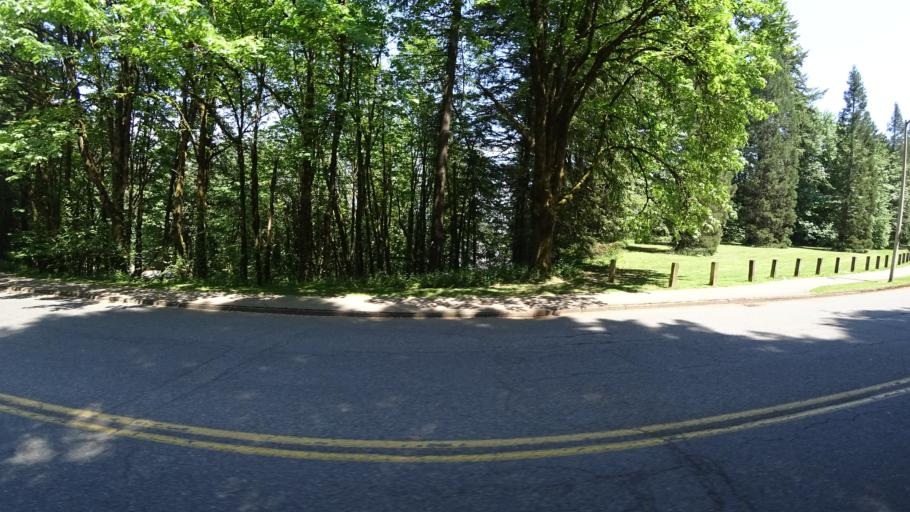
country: US
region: Oregon
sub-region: Multnomah County
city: Portland
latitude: 45.5003
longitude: -122.7075
